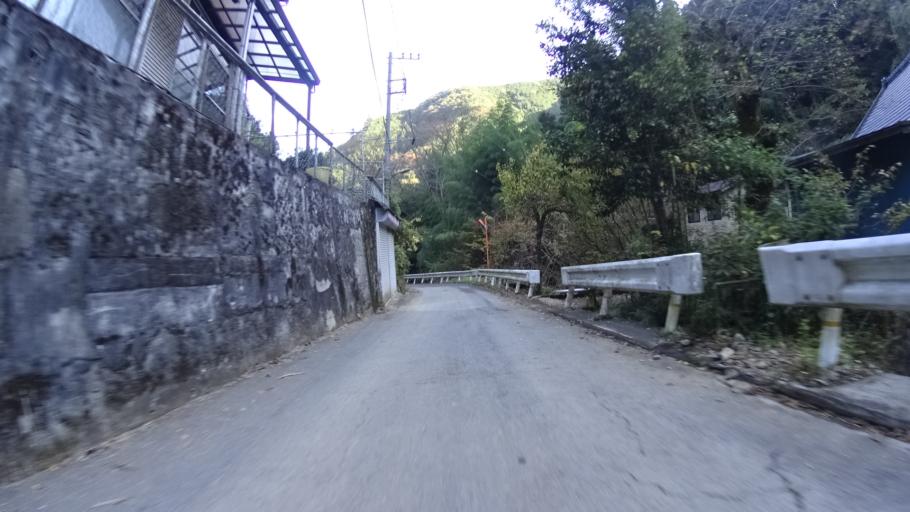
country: JP
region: Tokyo
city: Itsukaichi
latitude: 35.6641
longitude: 139.1871
